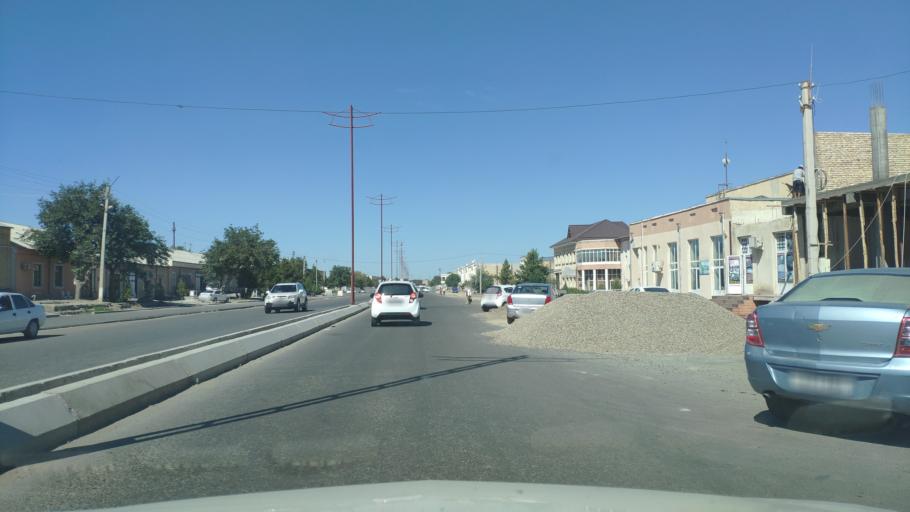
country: UZ
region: Bukhara
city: Bukhara
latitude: 39.7747
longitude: 64.3889
